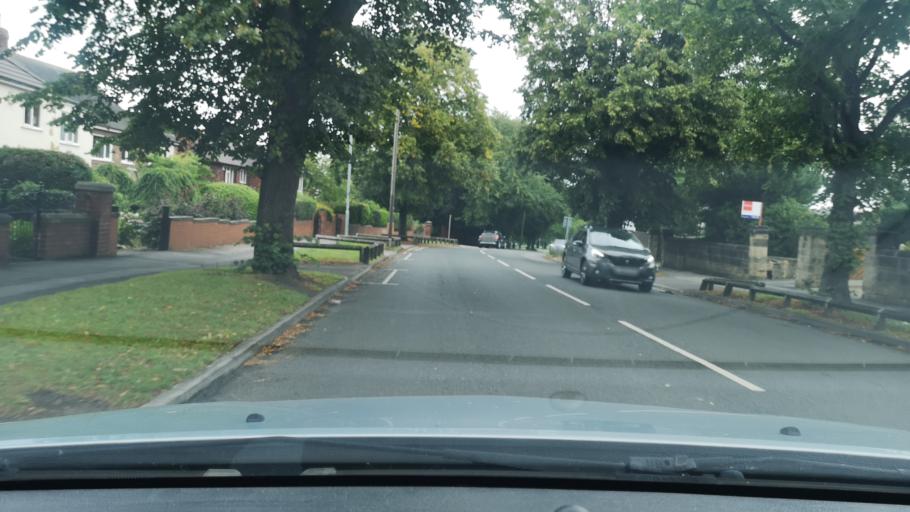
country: GB
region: England
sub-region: City and Borough of Wakefield
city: Wakefield
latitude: 53.6799
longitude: -1.5286
